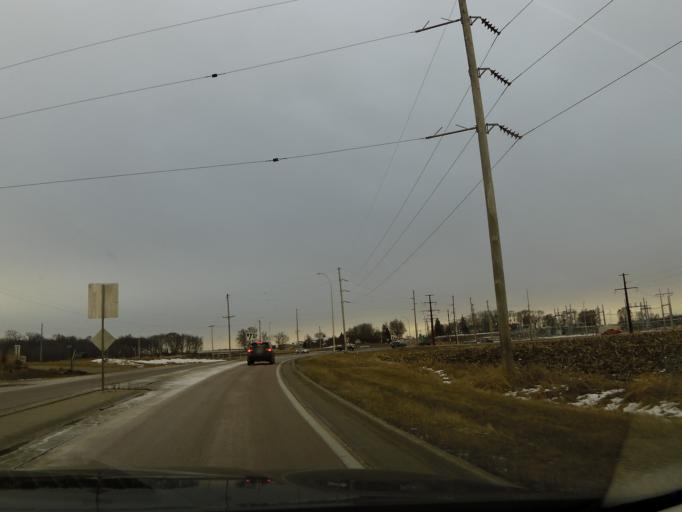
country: US
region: Minnesota
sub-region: Carver County
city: Watertown
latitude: 44.9068
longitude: -93.8191
